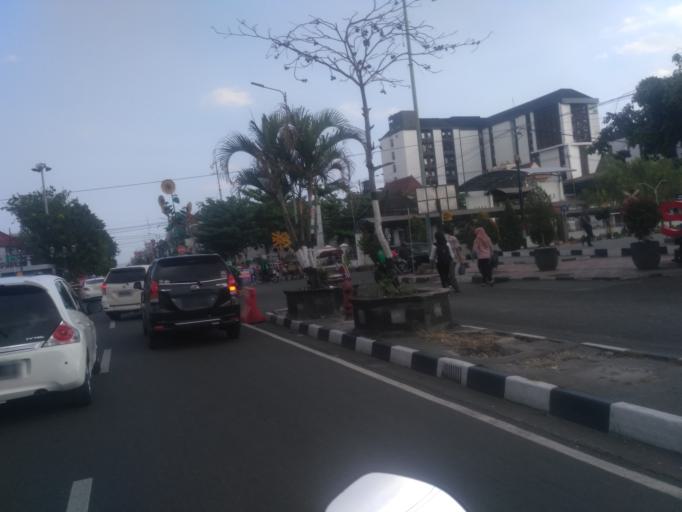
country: ID
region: Daerah Istimewa Yogyakarta
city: Yogyakarta
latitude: -7.7892
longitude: 110.3663
